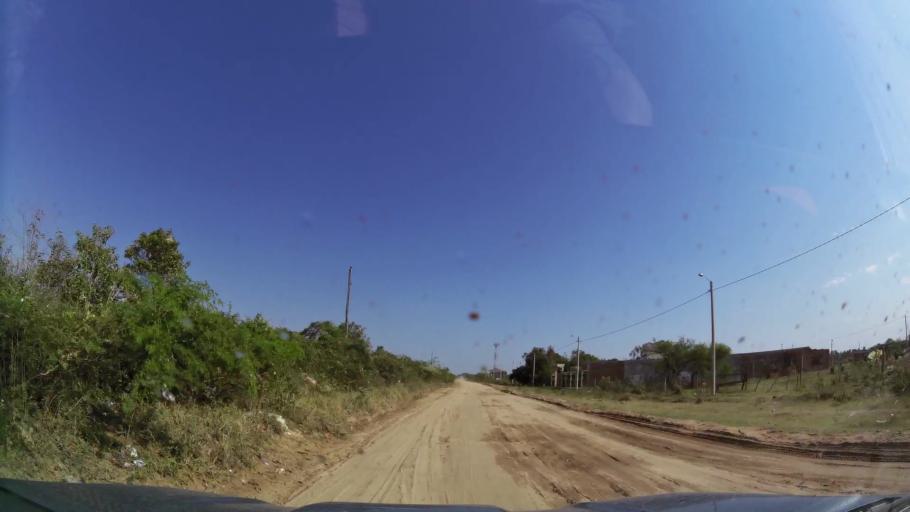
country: BO
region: Santa Cruz
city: Cotoca
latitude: -17.7245
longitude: -63.0694
